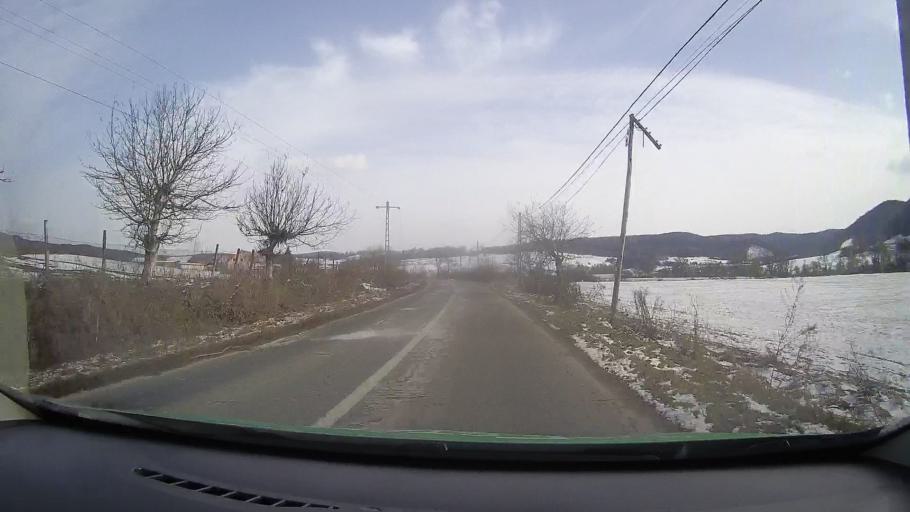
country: RO
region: Mures
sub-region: Comuna Apold
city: Saes
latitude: 46.1420
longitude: 24.7848
